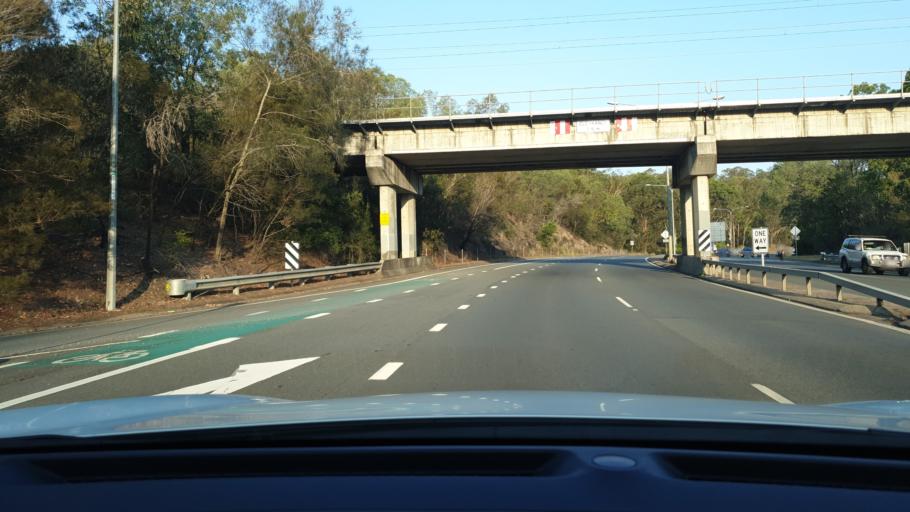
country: AU
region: Queensland
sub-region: Gold Coast
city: Nerang
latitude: -27.9819
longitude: 153.3465
